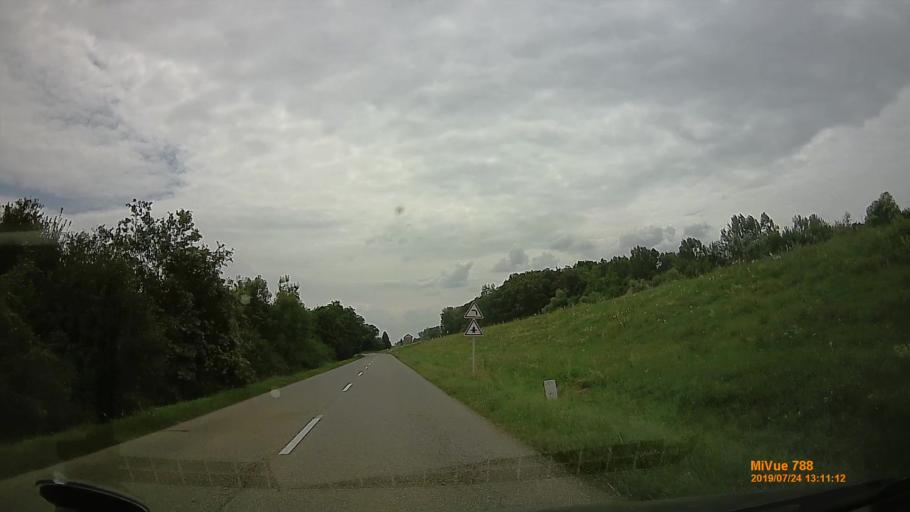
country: HU
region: Szabolcs-Szatmar-Bereg
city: Vasarosnameny
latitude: 48.1681
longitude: 22.3372
